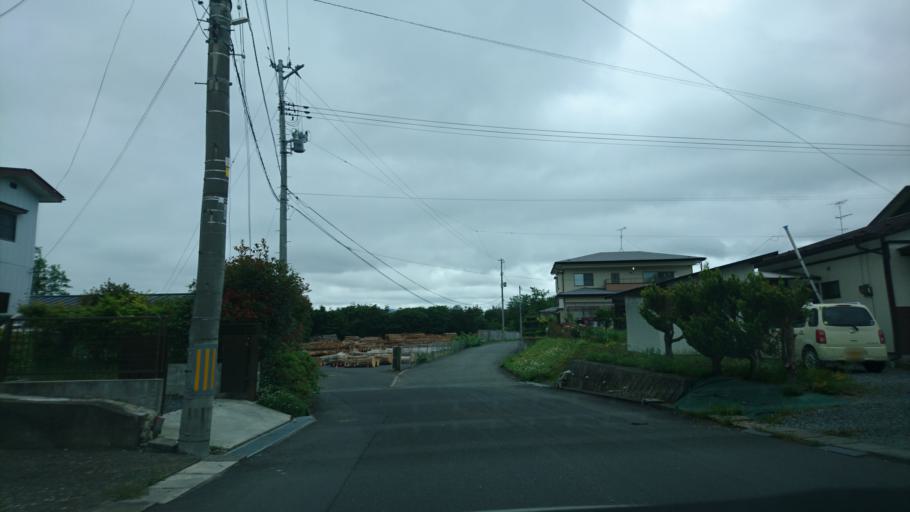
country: JP
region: Iwate
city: Ichinoseki
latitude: 38.9116
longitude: 141.1687
